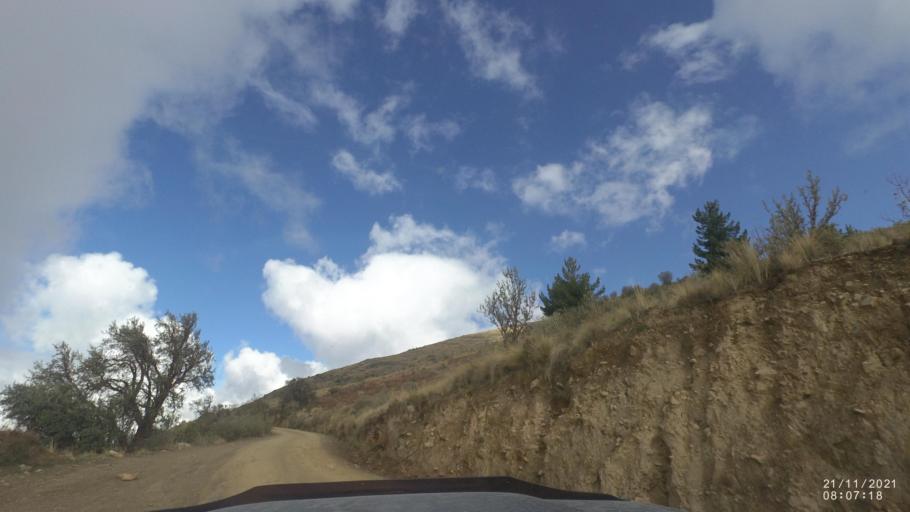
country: BO
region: Cochabamba
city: Cochabamba
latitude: -17.2870
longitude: -66.2109
